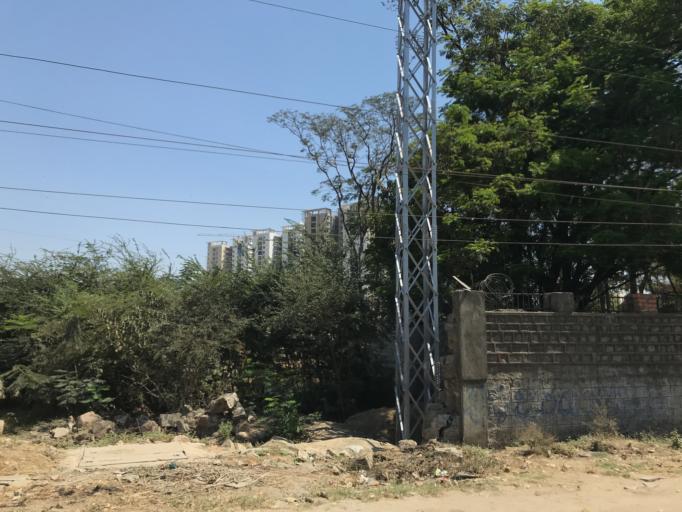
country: IN
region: Telangana
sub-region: Medak
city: Serilingampalle
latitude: 17.4681
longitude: 78.3313
